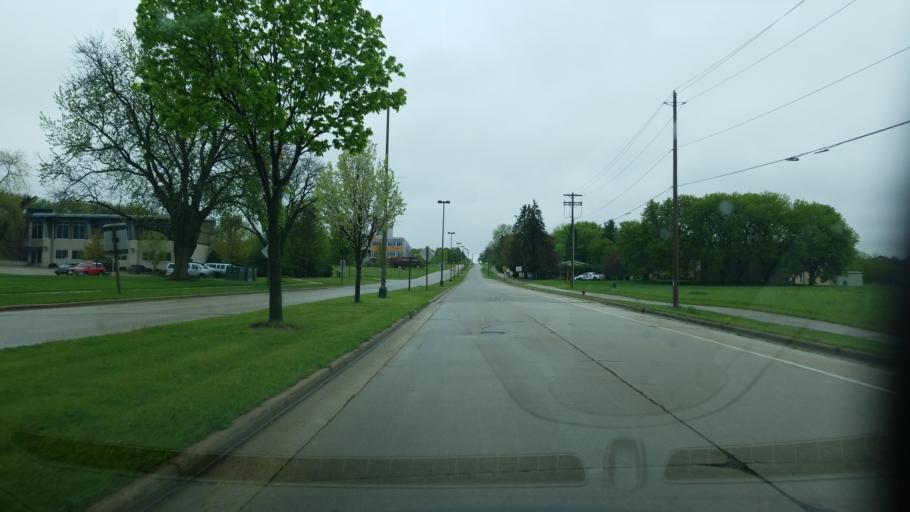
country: US
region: Wisconsin
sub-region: Dane County
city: Fitchburg
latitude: 43.0003
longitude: -89.4281
